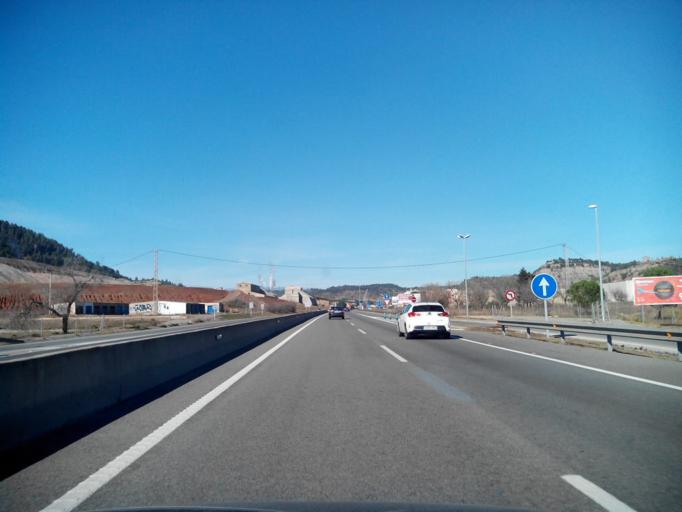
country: ES
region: Catalonia
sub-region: Provincia de Barcelona
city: Sallent
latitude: 41.8056
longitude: 1.8977
